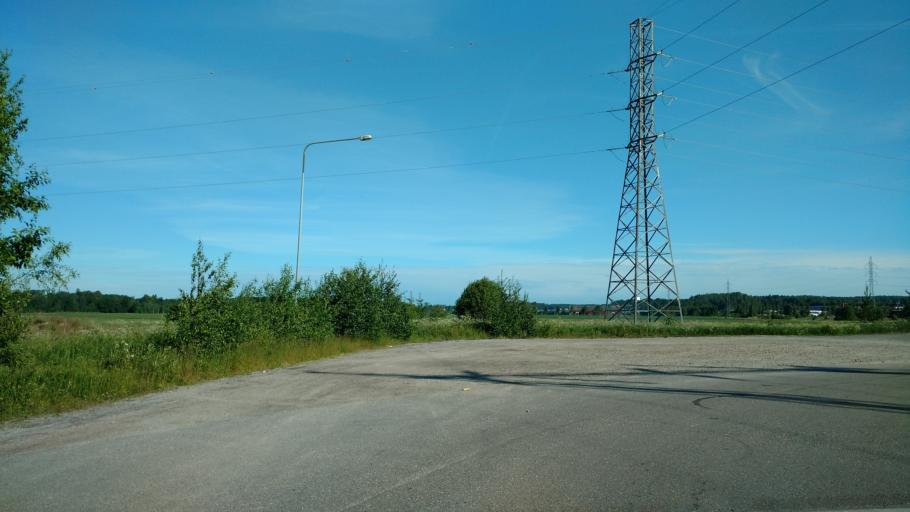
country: FI
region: Varsinais-Suomi
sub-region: Salo
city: Halikko
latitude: 60.3765
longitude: 23.1029
